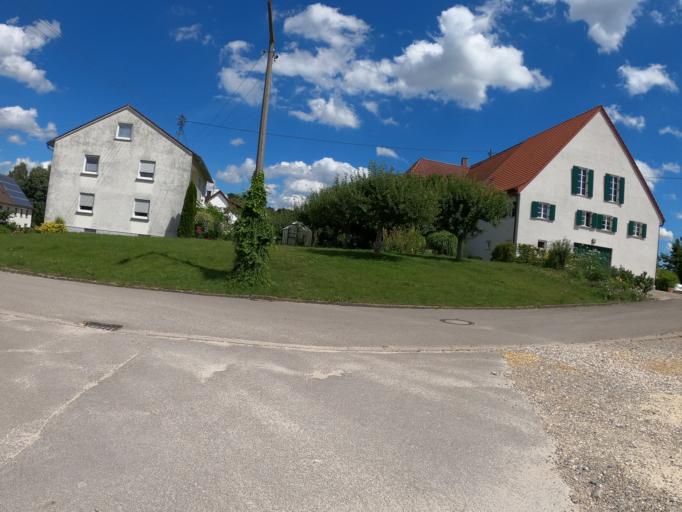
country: DE
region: Bavaria
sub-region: Swabia
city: Pfaffenhofen an der Roth
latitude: 48.3996
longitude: 10.1858
